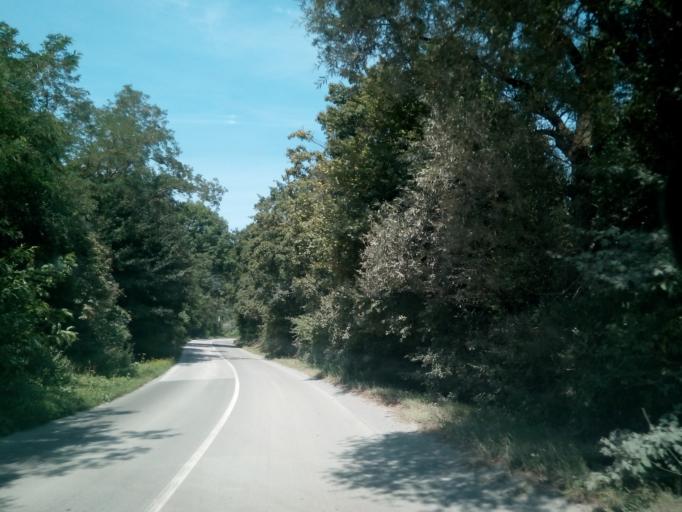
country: SK
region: Kosicky
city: Kosice
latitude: 48.8304
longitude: 21.2204
